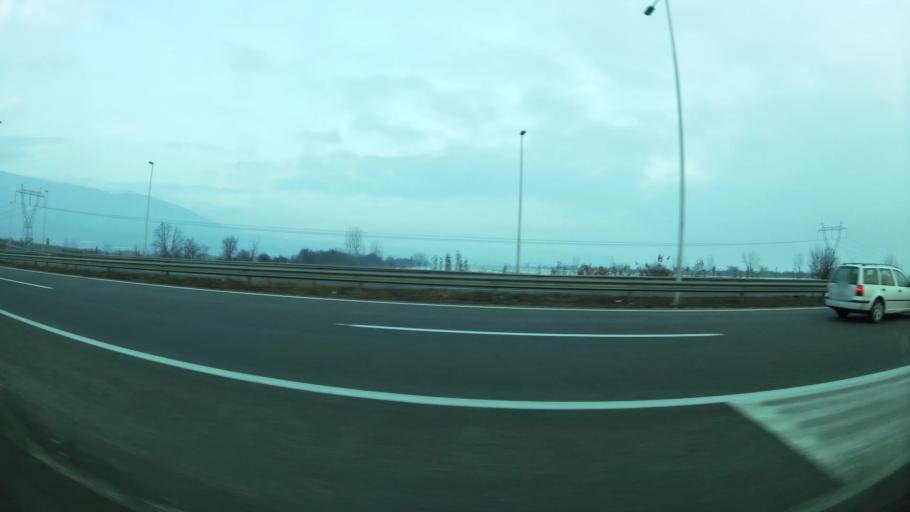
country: MK
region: Aracinovo
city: Arachinovo
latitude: 42.0165
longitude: 21.5340
